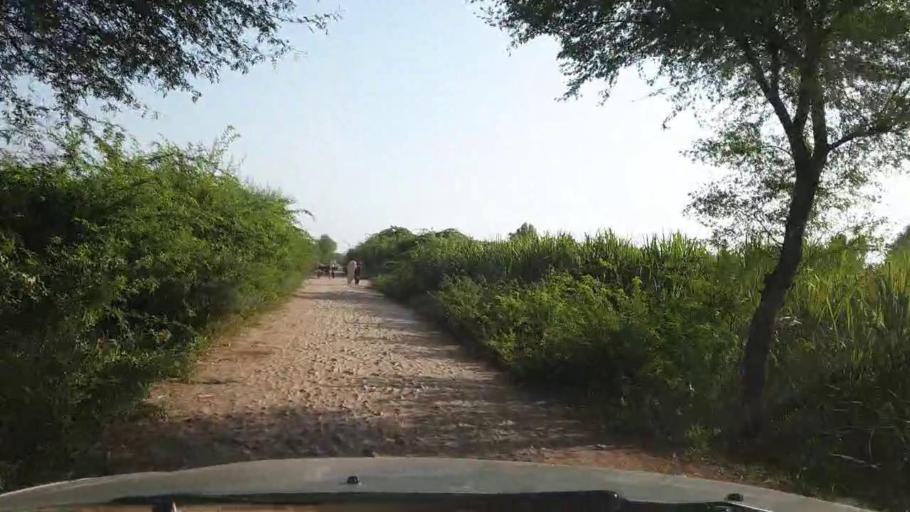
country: PK
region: Sindh
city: Tando Ghulam Ali
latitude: 25.1408
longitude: 68.9428
